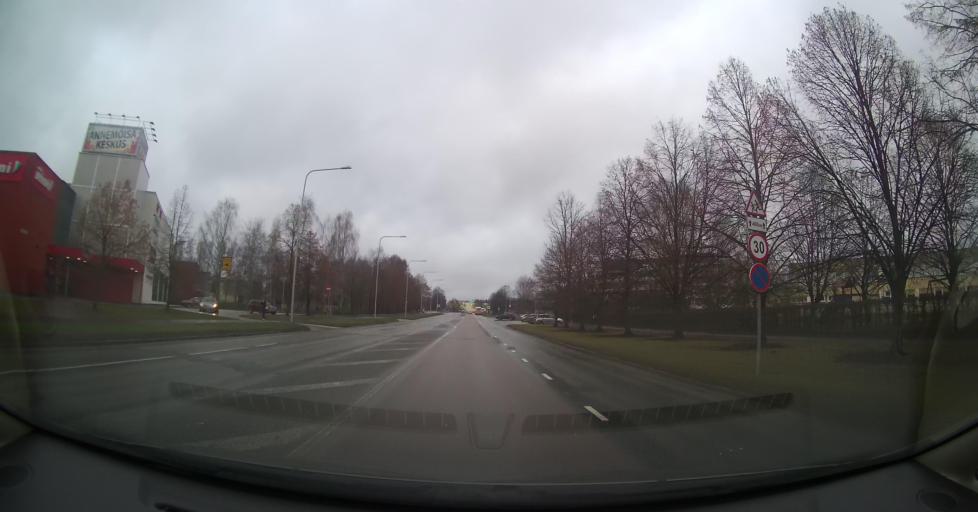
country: EE
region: Tartu
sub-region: Tartu linn
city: Tartu
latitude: 58.3739
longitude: 26.7684
